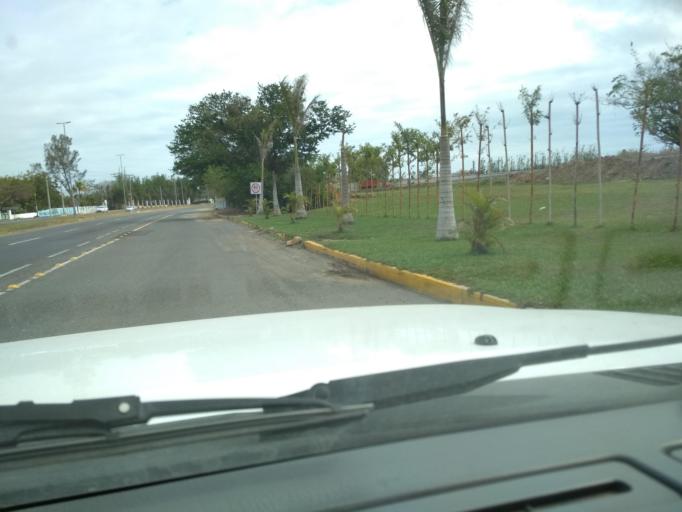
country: MX
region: Veracruz
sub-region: Alvarado
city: Playa de la Libertad
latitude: 19.0879
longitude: -96.1177
